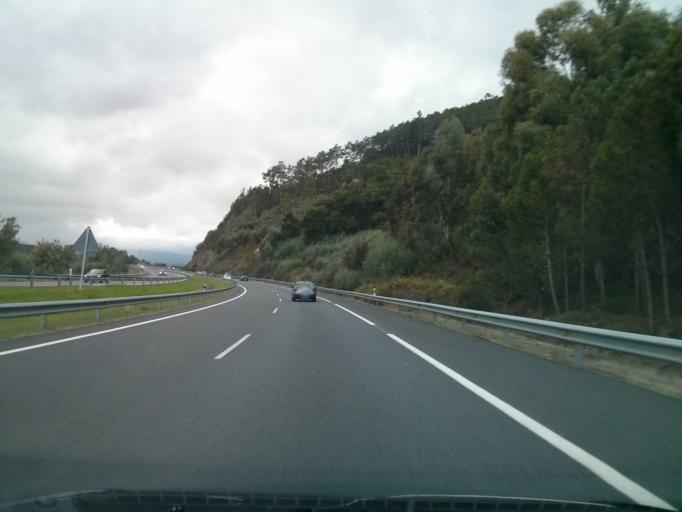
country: ES
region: Galicia
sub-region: Provincia de Ourense
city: Punxin
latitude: 42.3351
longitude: -8.0276
